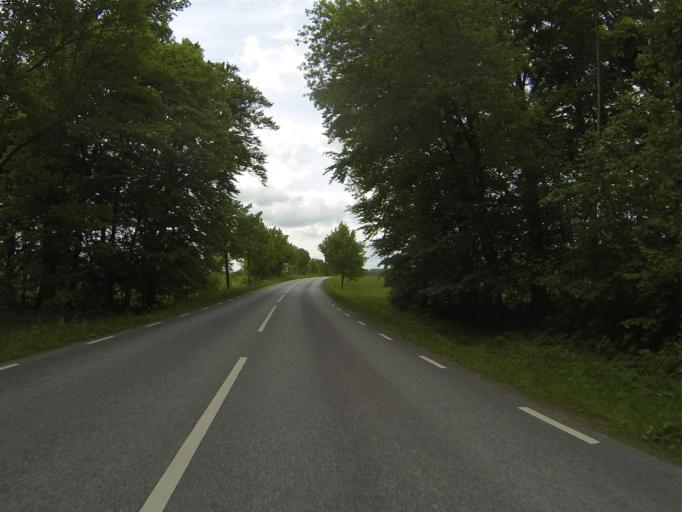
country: SE
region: Skane
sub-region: Sjobo Kommun
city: Sjoebo
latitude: 55.6675
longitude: 13.6694
